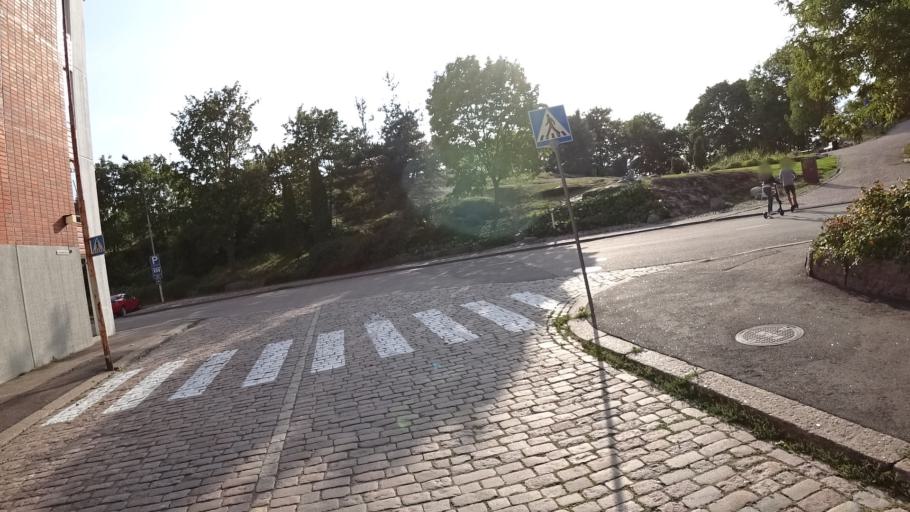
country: FI
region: Kymenlaakso
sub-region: Kotka-Hamina
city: Kotka
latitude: 60.4674
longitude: 26.9414
